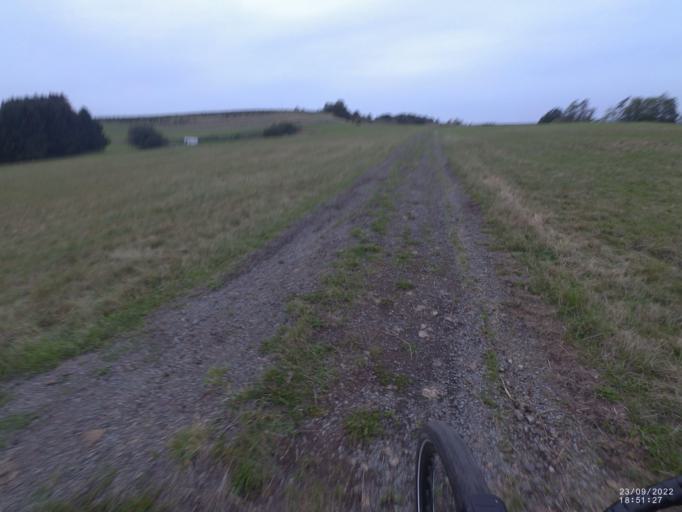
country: DE
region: Rheinland-Pfalz
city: Dockweiler
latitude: 50.2405
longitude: 6.7927
